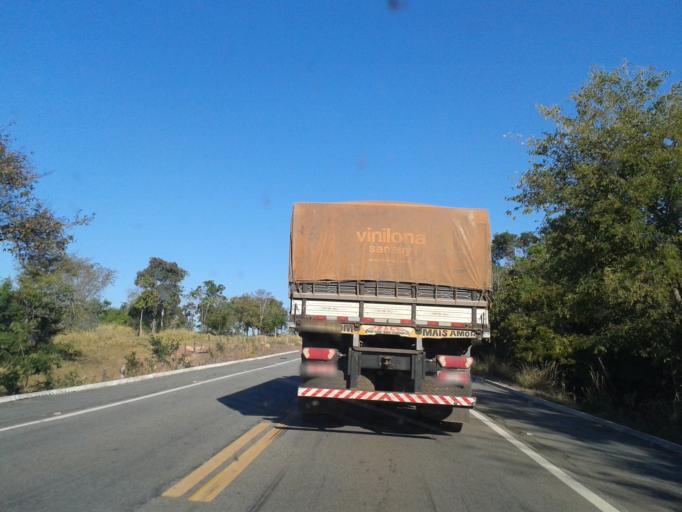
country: BR
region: Goias
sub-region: Mozarlandia
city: Mozarlandia
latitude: -15.2150
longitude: -50.5328
